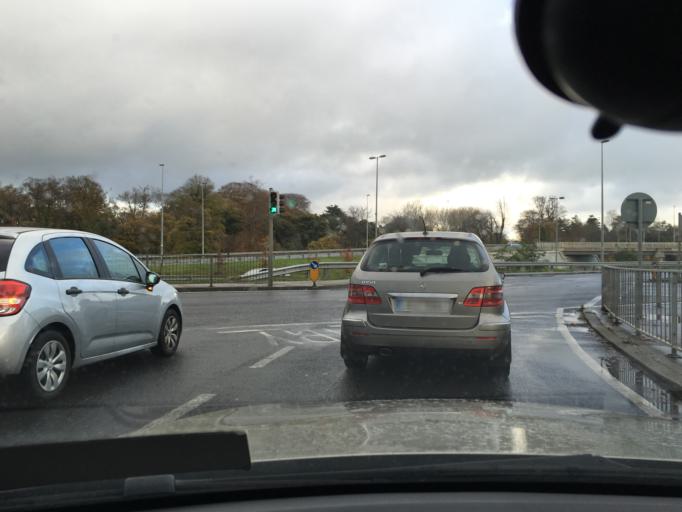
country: IE
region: Leinster
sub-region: Fingal County
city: Blanchardstown
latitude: 53.3852
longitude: -6.3688
